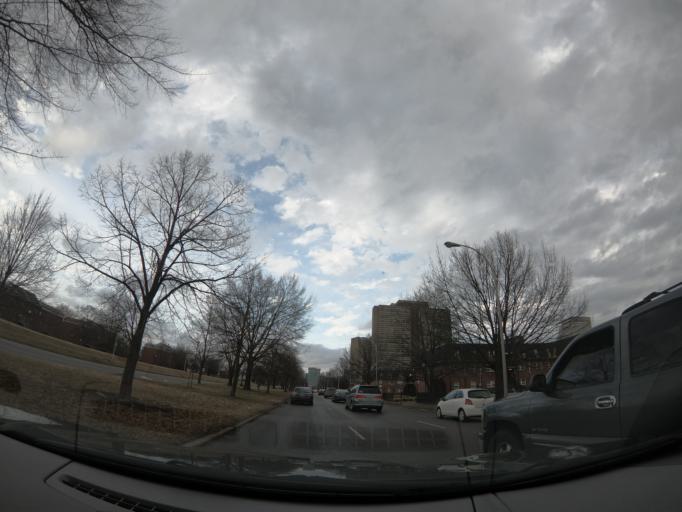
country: US
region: Kentucky
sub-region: Jefferson County
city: Louisville
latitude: 38.2501
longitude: -85.7659
